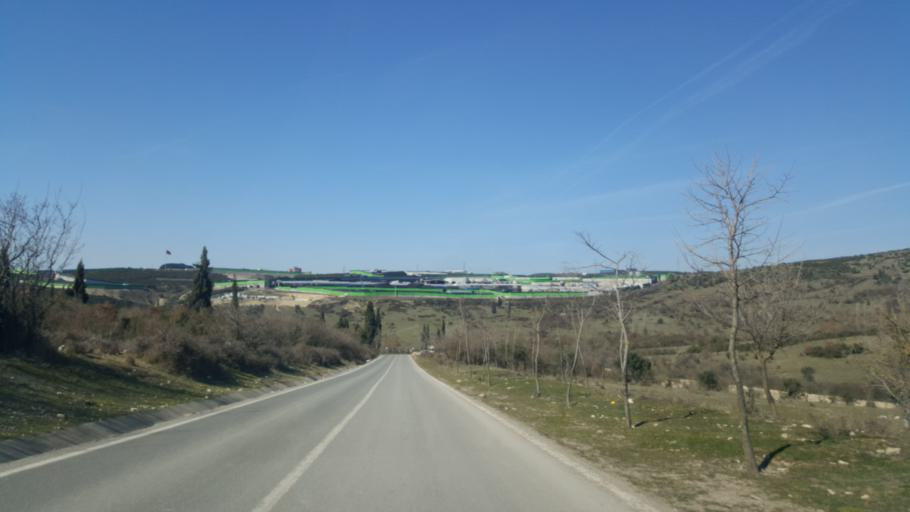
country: TR
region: Kocaeli
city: Tavsancil
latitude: 40.7854
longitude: 29.5731
